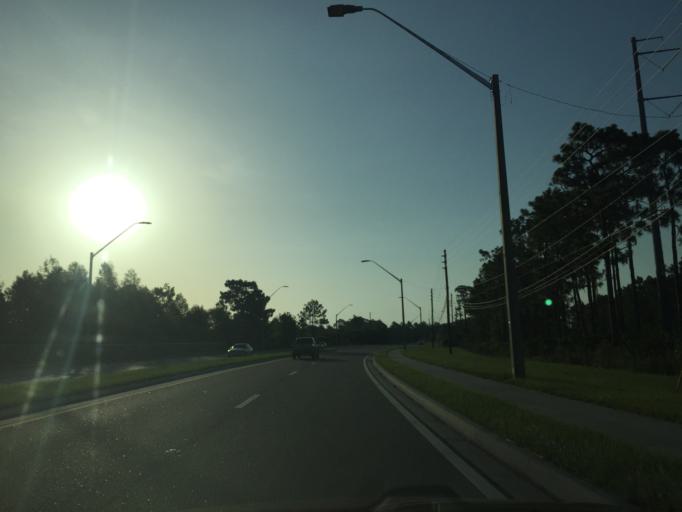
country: US
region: Florida
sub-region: Orange County
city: Alafaya
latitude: 28.5109
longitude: -81.1711
